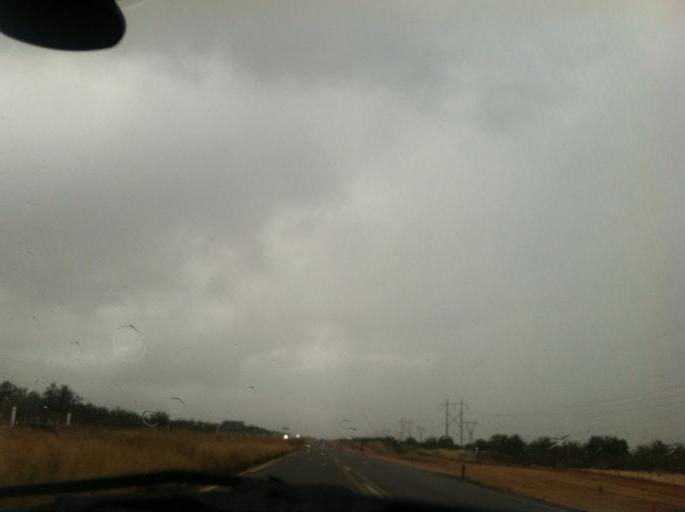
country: MX
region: Sonora
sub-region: San Miguel de Horcasitas
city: Las Mercedes [Agropecuaria]
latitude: 29.3737
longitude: -110.9728
